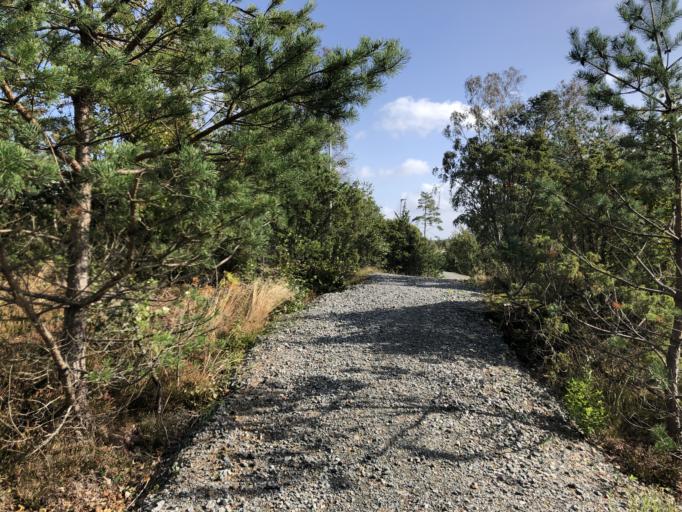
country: SE
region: Vaestra Goetaland
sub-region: Goteborg
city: Torslanda
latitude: 57.7393
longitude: 11.8356
